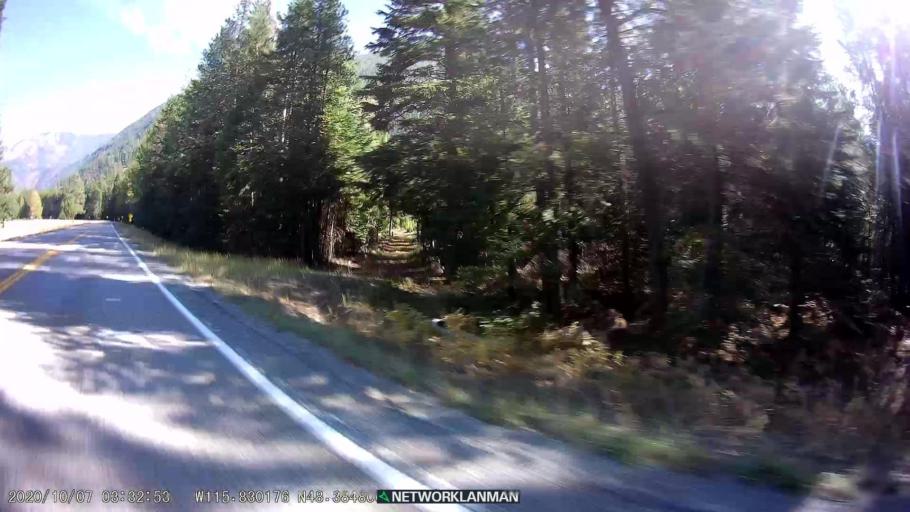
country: US
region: Montana
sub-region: Lincoln County
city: Libby
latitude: 48.3849
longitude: -115.8292
